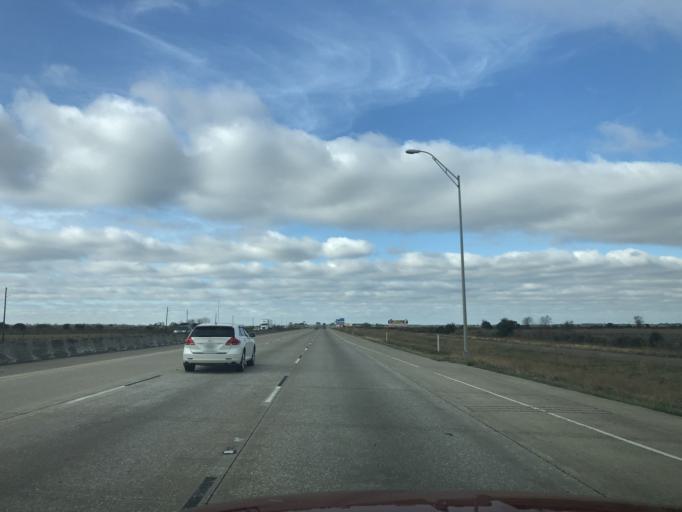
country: US
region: Texas
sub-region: Chambers County
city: Winnie
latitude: 29.8332
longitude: -94.5209
